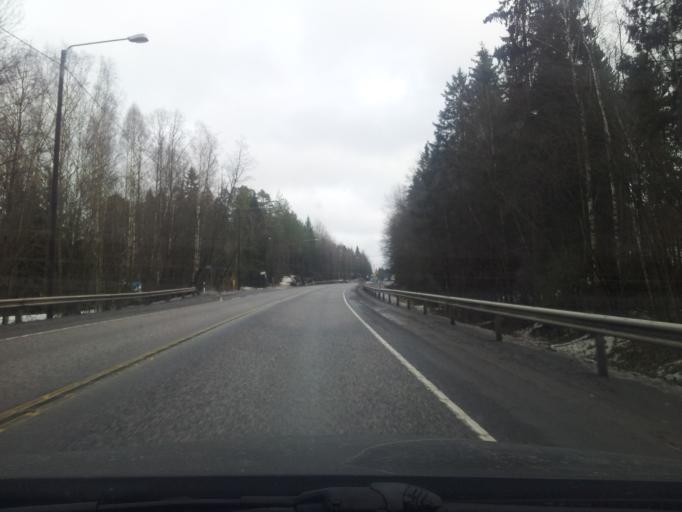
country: FI
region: Uusimaa
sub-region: Helsinki
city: Espoo
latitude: 60.2031
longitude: 24.6038
